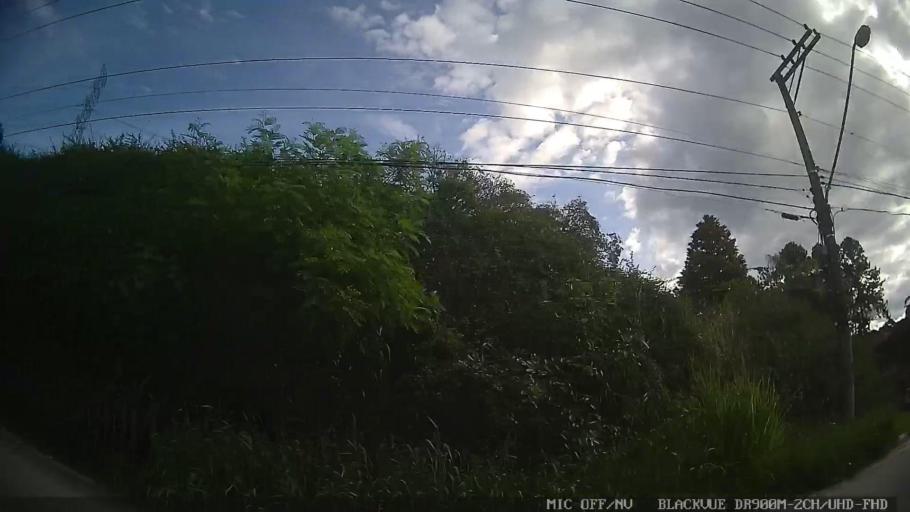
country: BR
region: Sao Paulo
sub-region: Mogi das Cruzes
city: Mogi das Cruzes
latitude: -23.5325
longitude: -46.1584
